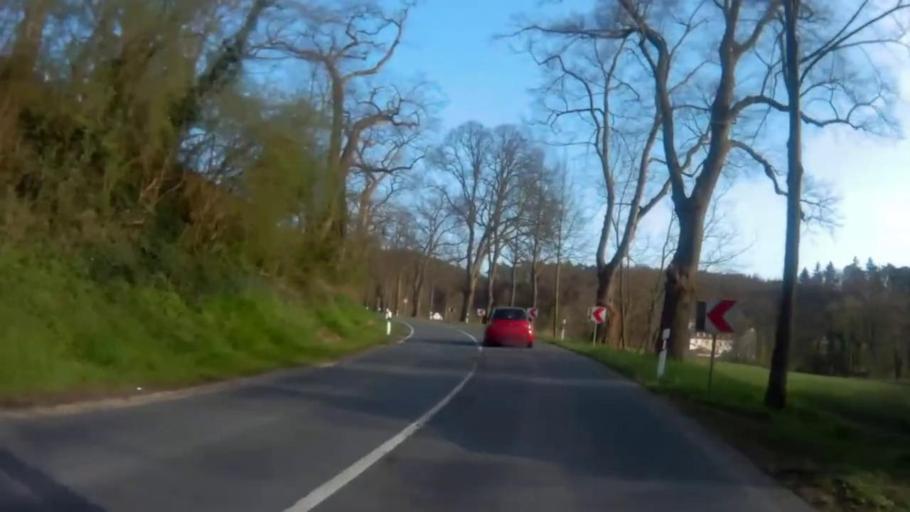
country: DE
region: Hesse
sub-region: Regierungsbezirk Darmstadt
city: Darmstadt
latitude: 49.8197
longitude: 8.6667
